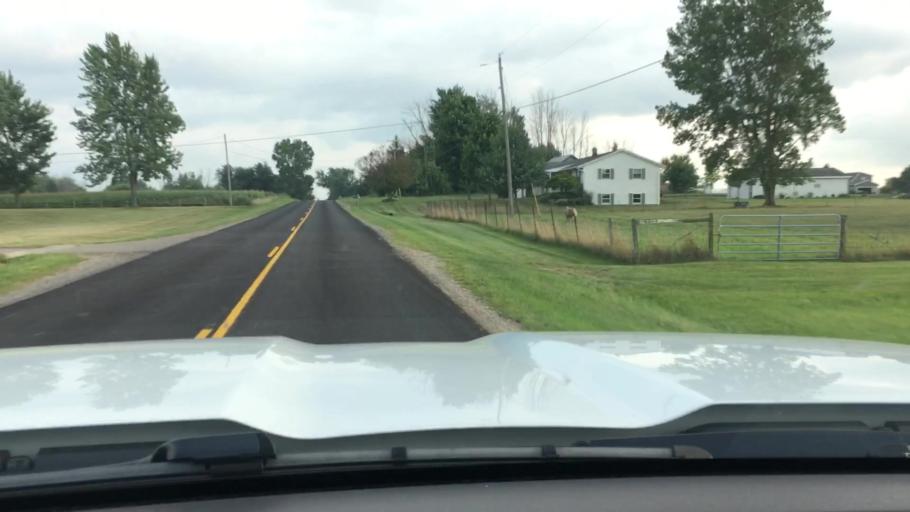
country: US
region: Michigan
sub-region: Ottawa County
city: Hudsonville
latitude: 42.8305
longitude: -85.8816
